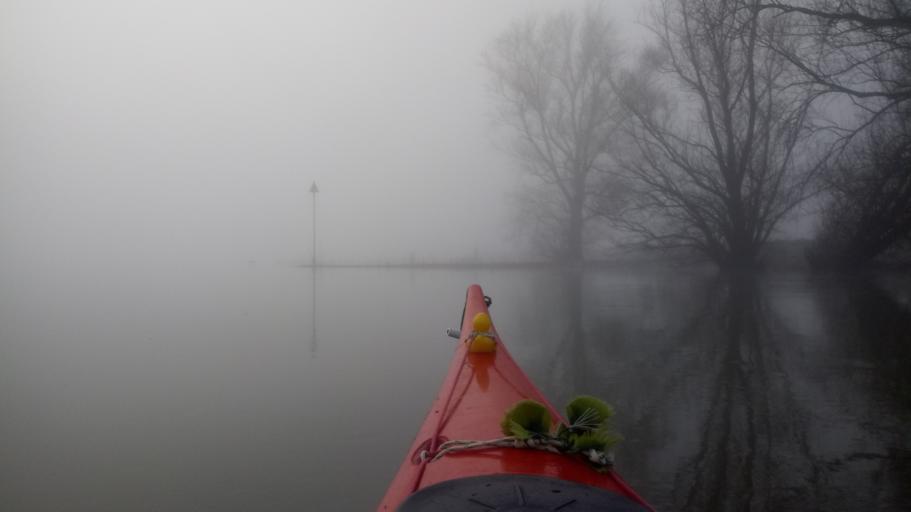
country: NL
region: Gelderland
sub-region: Gemeente Rheden
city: Spankeren
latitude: 52.0564
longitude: 6.1325
